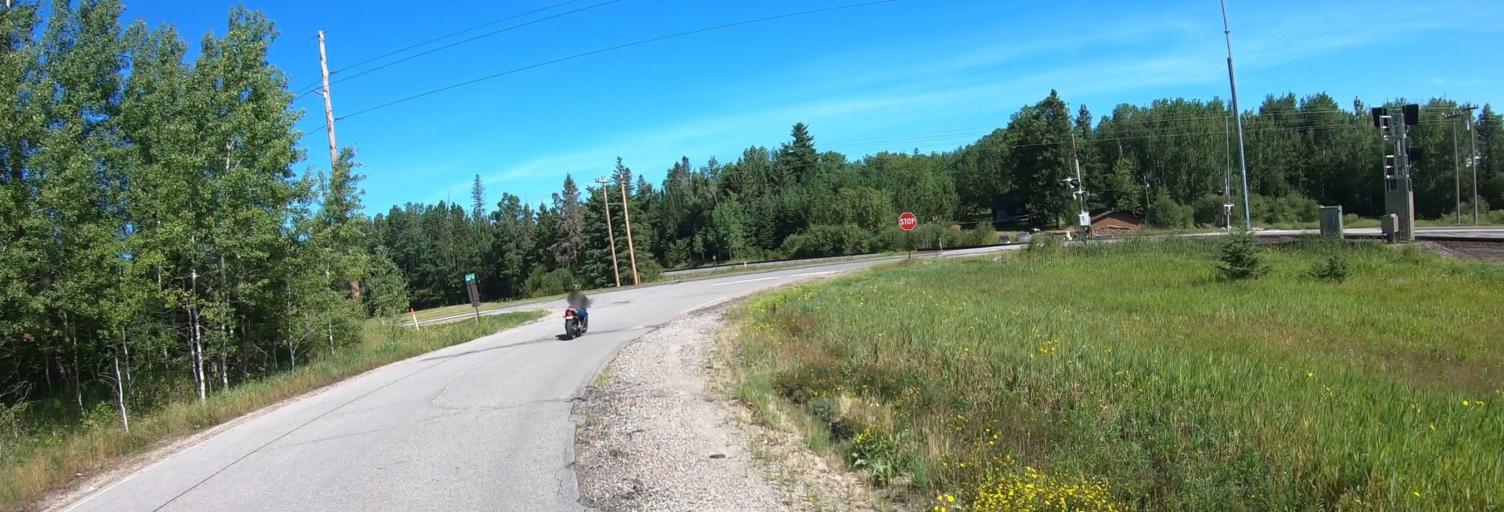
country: US
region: Minnesota
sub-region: Saint Louis County
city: Mountain Iron
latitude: 47.8603
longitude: -92.6971
